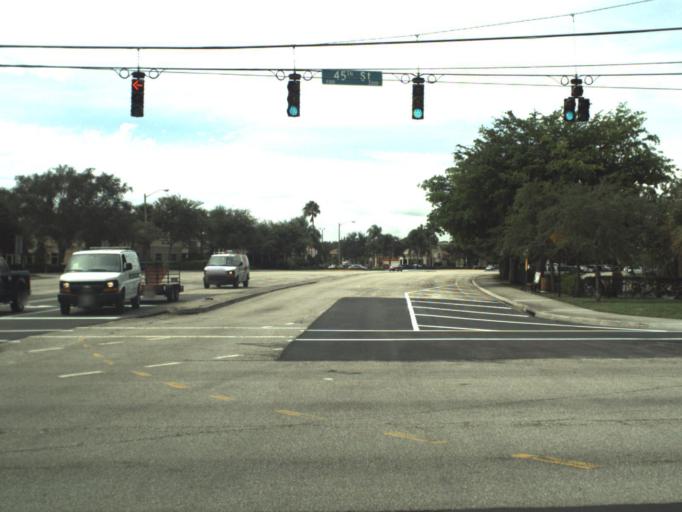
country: US
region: Florida
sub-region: Palm Beach County
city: Mangonia Park
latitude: 26.7589
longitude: -80.0865
